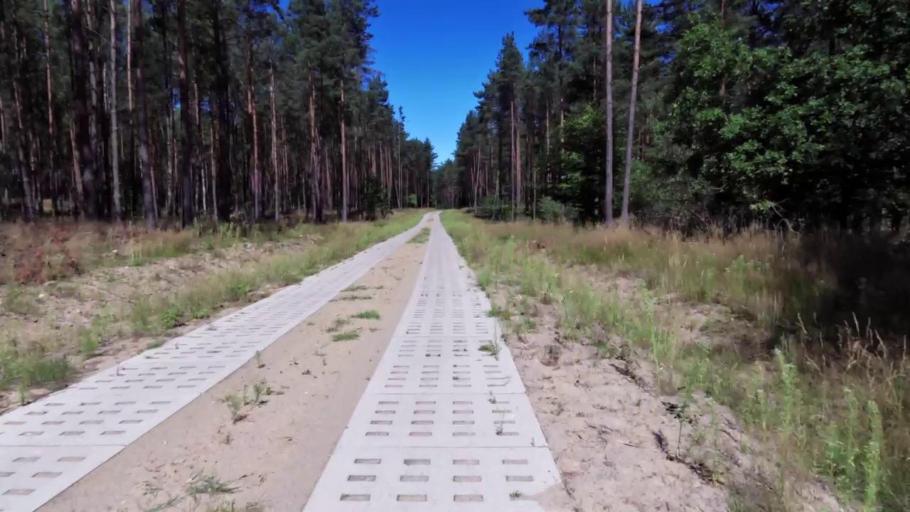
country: PL
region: West Pomeranian Voivodeship
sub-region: Powiat szczecinecki
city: Szczecinek
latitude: 53.6247
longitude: 16.6615
